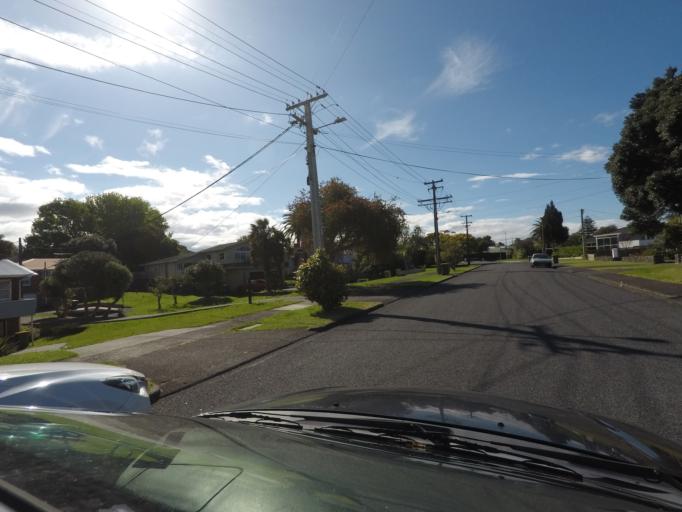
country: NZ
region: Auckland
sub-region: Auckland
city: Rosebank
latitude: -36.8620
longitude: 174.6546
